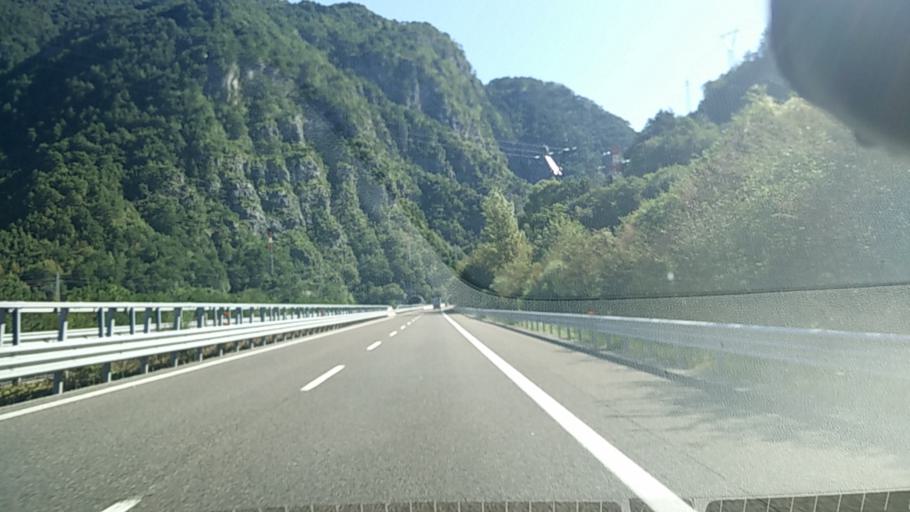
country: IT
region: Friuli Venezia Giulia
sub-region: Provincia di Udine
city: Resiutta
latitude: 46.3953
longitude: 13.2619
